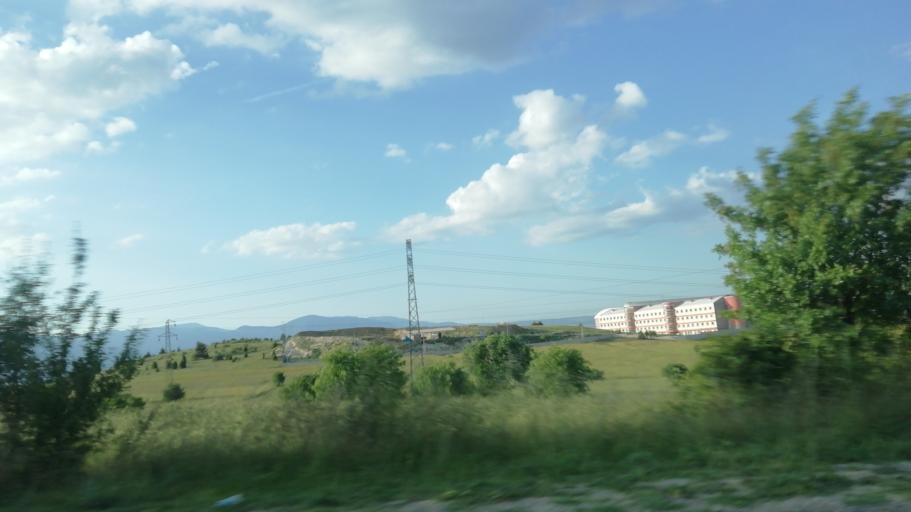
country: TR
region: Karabuk
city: Karabuk
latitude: 41.1328
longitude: 32.6270
